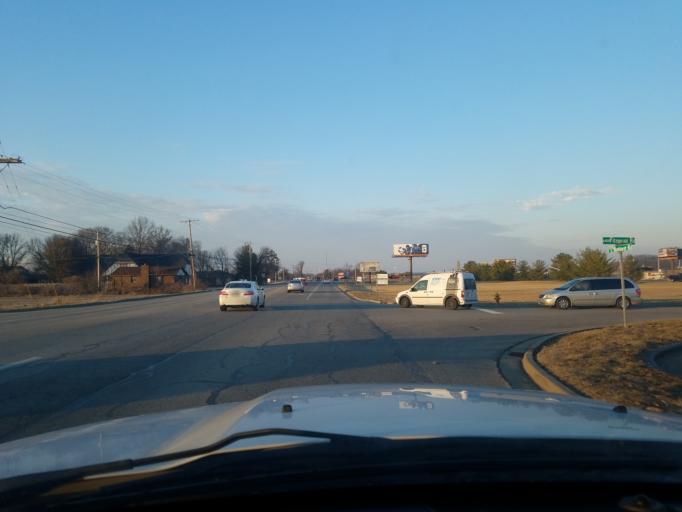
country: US
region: Indiana
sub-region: Vanderburgh County
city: Melody Hill
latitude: 38.0102
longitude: -87.4736
